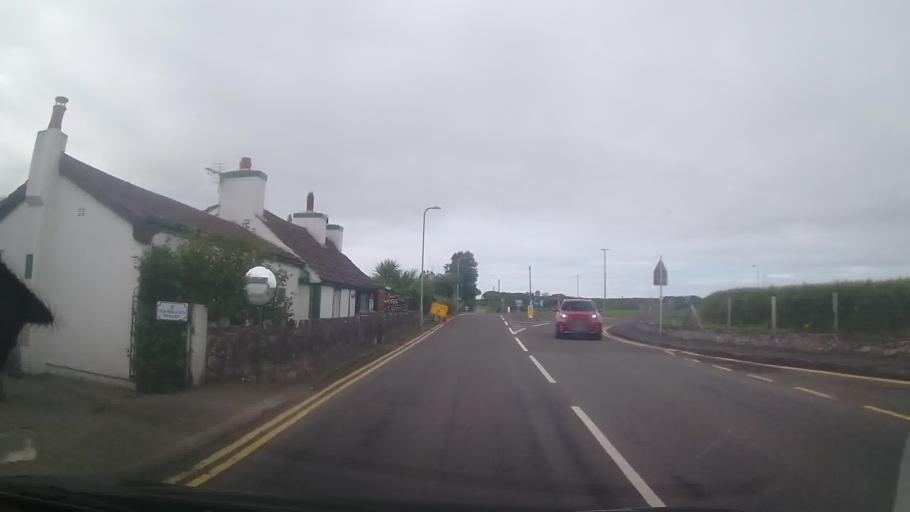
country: GB
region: Wales
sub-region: Gwynedd
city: Caernarfon
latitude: 53.1596
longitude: -4.3490
